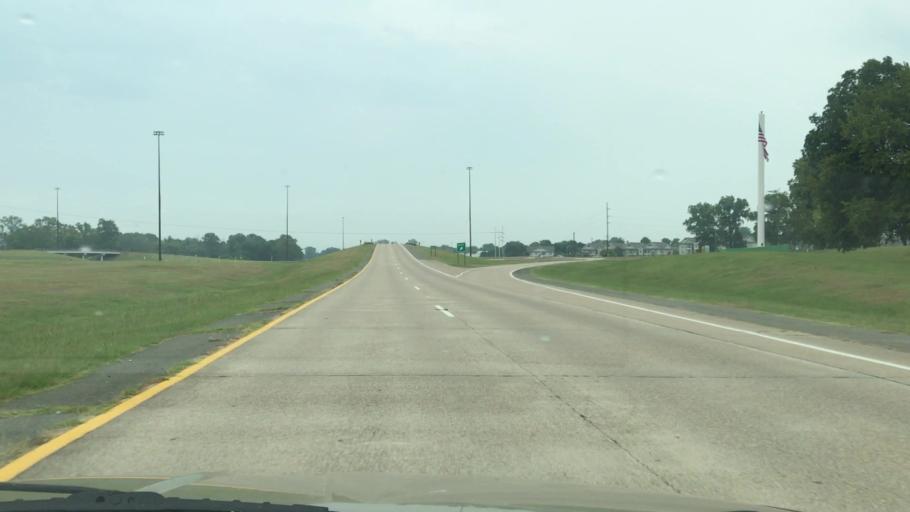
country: US
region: Louisiana
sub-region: Bossier Parish
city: Bossier City
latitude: 32.5024
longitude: -93.7183
